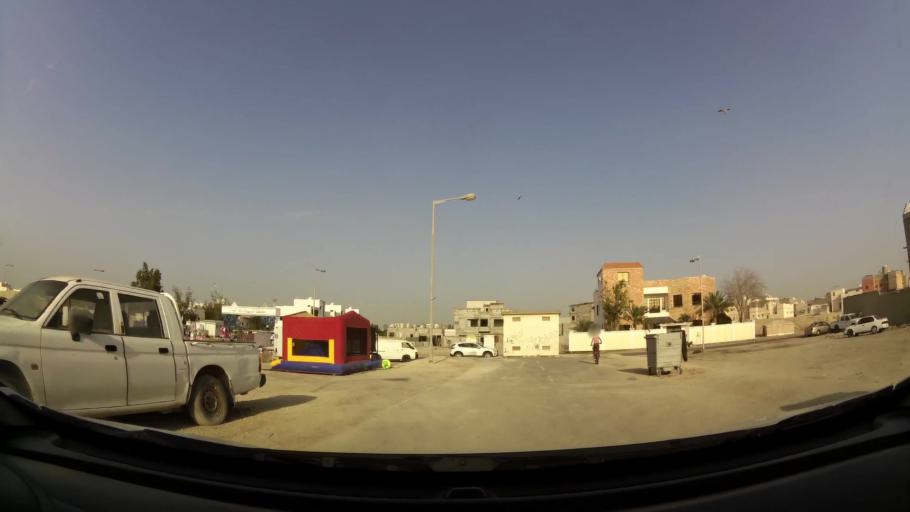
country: BH
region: Manama
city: Jidd Hafs
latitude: 26.2164
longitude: 50.4992
